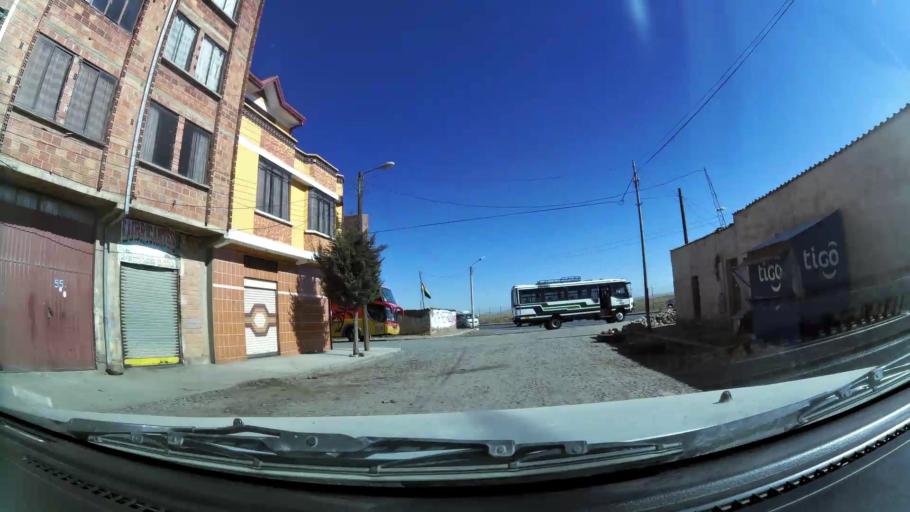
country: BO
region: La Paz
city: La Paz
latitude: -16.5165
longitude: -68.1751
